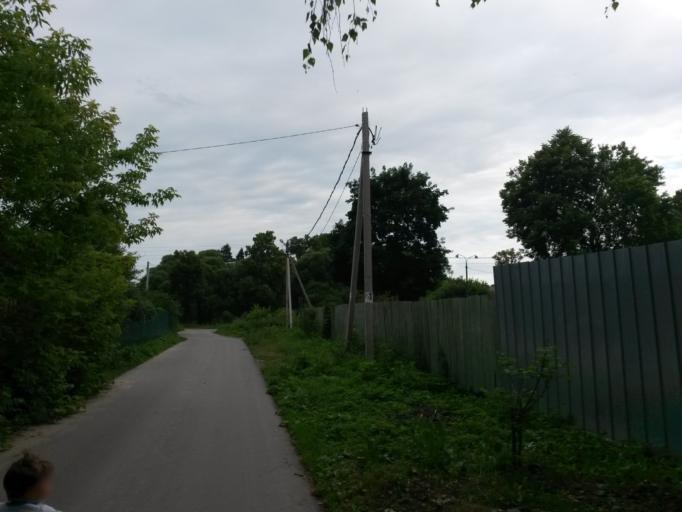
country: RU
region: Moskovskaya
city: Lyubuchany
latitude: 55.2526
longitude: 37.6132
